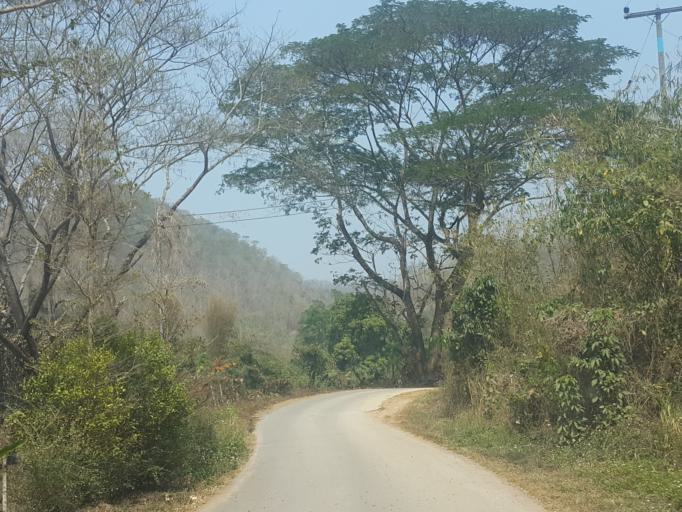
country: TH
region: Chiang Mai
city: Hang Dong
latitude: 18.7263
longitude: 98.8335
